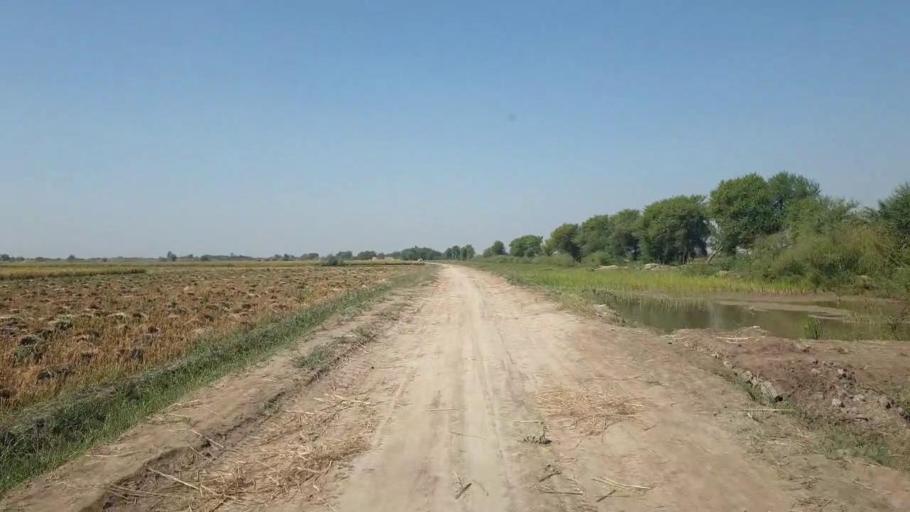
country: PK
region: Sindh
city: Talhar
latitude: 24.8049
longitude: 68.8072
